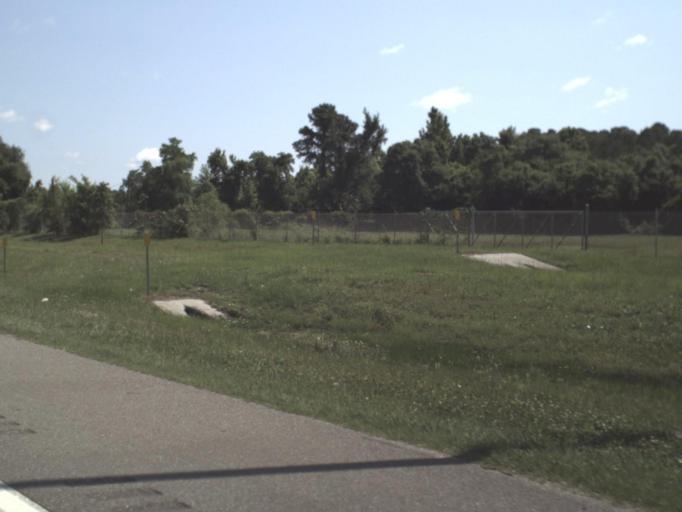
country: US
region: Florida
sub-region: Duval County
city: Jacksonville
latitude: 30.4198
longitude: -81.6566
